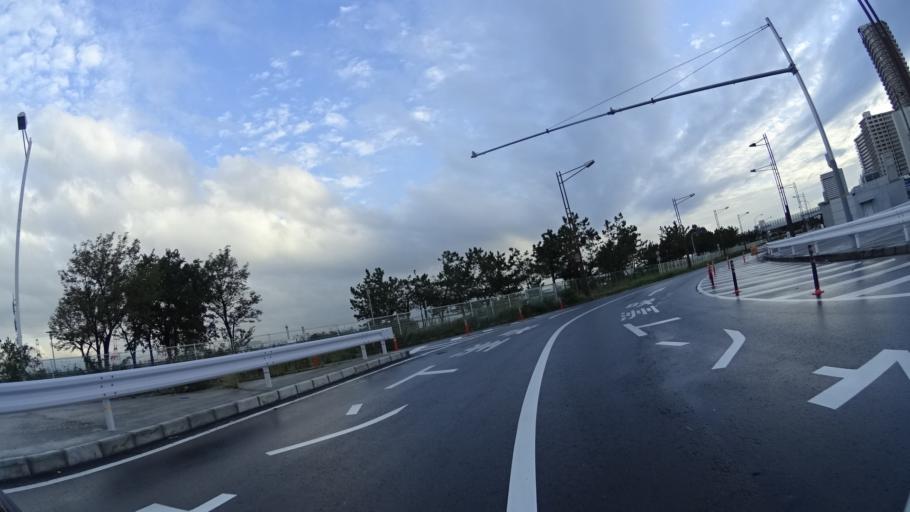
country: JP
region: Hyogo
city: Amagasaki
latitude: 34.6418
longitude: 135.4099
